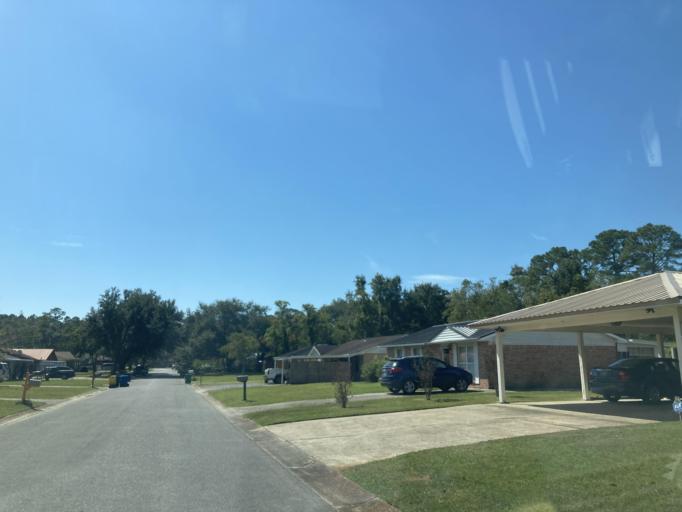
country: US
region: Mississippi
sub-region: Jackson County
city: Saint Martin
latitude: 30.4528
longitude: -88.8683
